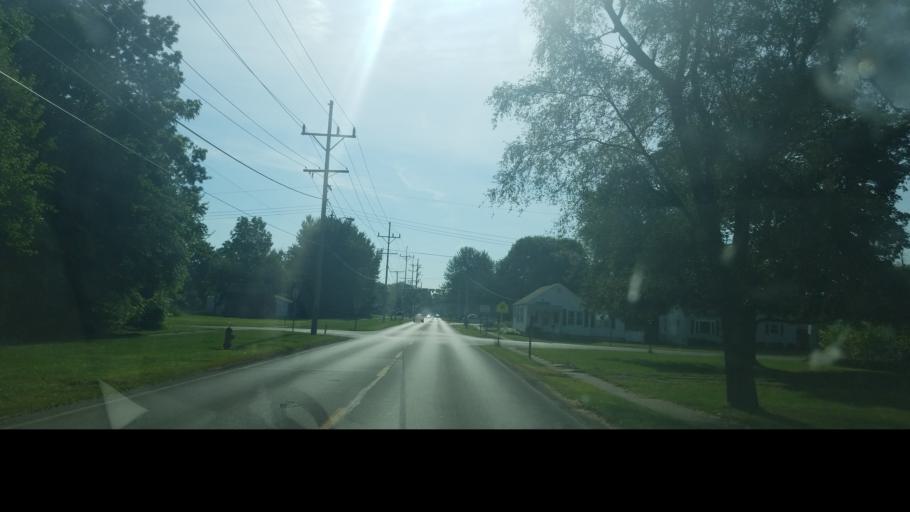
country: US
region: Ohio
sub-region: Hancock County
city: Findlay
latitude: 41.0223
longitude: -83.6463
